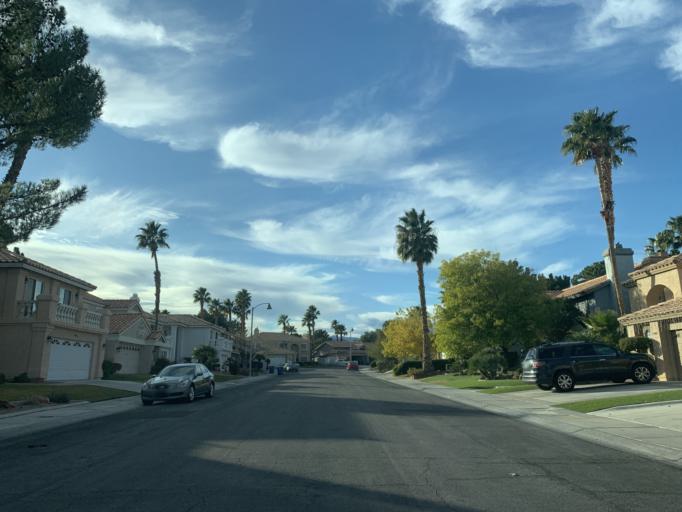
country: US
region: Nevada
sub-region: Clark County
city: Summerlin South
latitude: 36.1340
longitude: -115.2996
